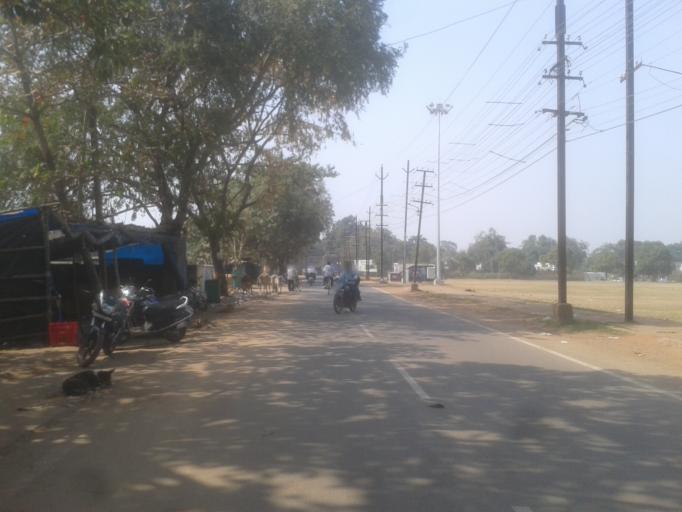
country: IN
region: Odisha
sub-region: Cuttack
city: Cuttack
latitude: 20.4828
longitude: 85.8667
